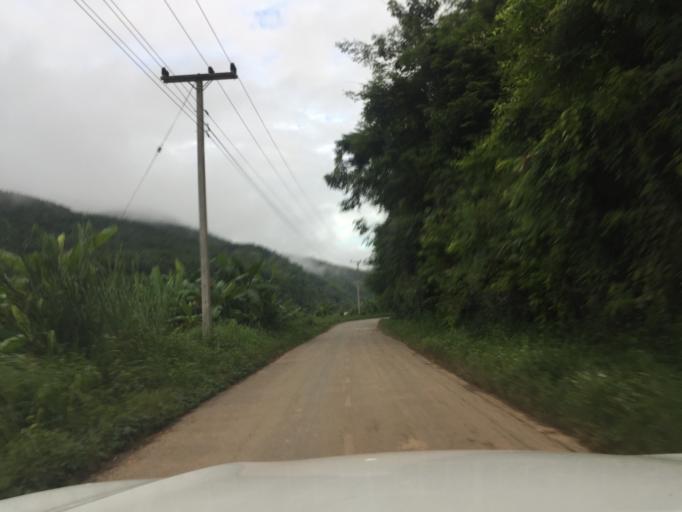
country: LA
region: Phongsali
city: Khoa
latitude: 21.0786
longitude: 102.3759
